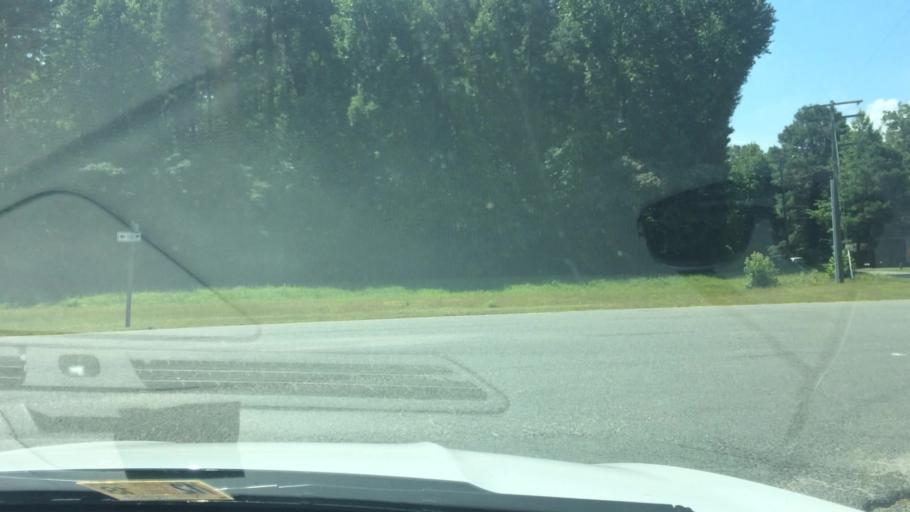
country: US
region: Virginia
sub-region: King William County
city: West Point
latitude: 37.5608
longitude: -76.8211
